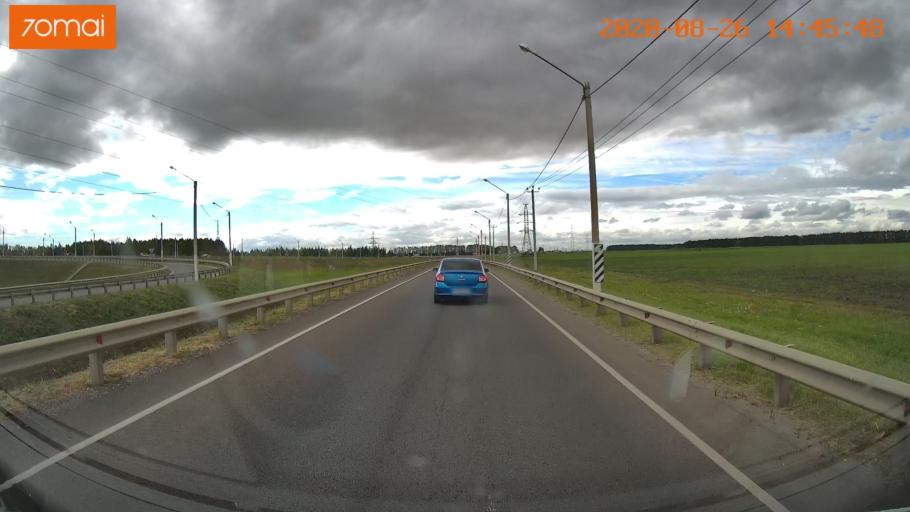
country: RU
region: Rjazan
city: Mikhaylov
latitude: 54.2477
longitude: 39.0546
